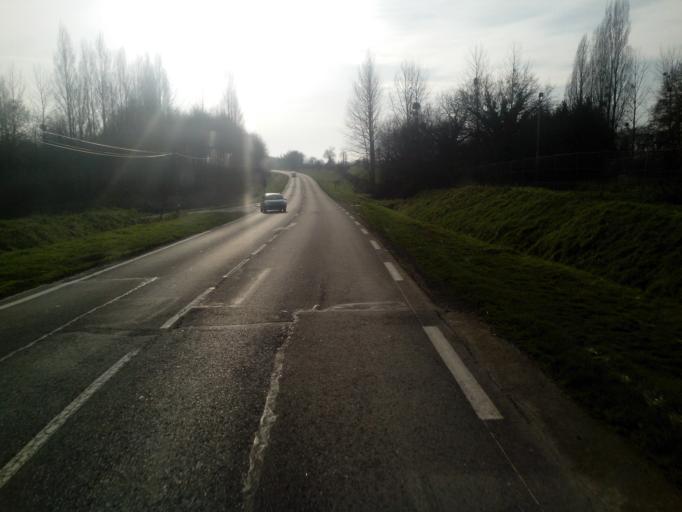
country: FR
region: Brittany
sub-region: Departement d'Ille-et-Vilaine
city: Saint-Meen-le-Grand
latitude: 48.1734
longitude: -2.2057
